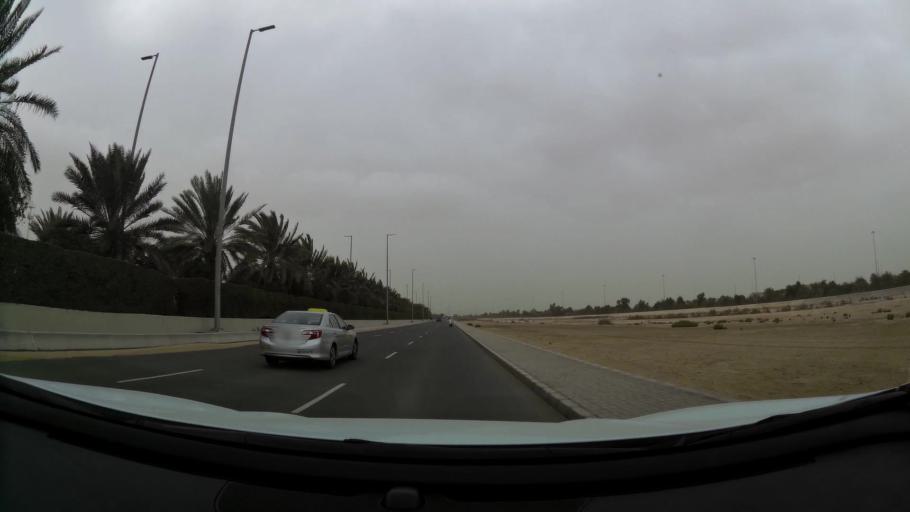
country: AE
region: Abu Dhabi
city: Abu Dhabi
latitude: 24.4245
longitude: 54.5353
